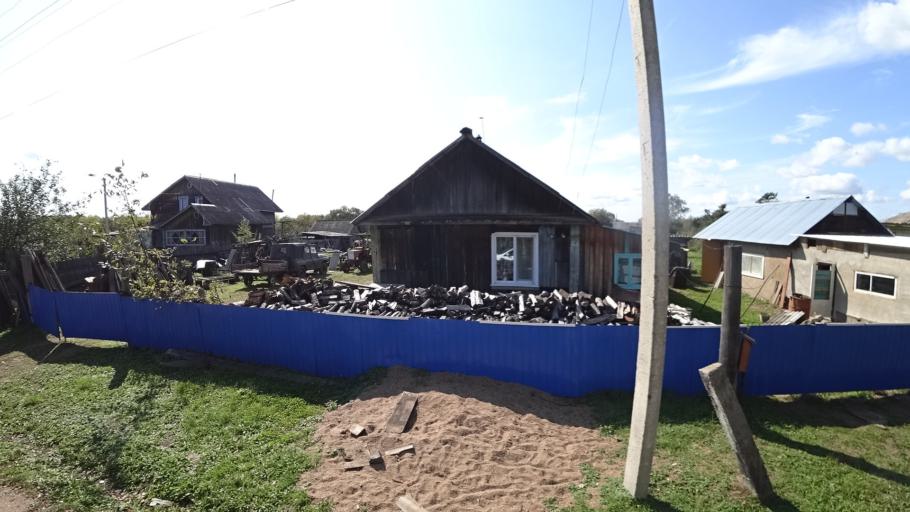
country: RU
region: Amur
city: Arkhara
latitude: 49.4003
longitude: 130.1498
